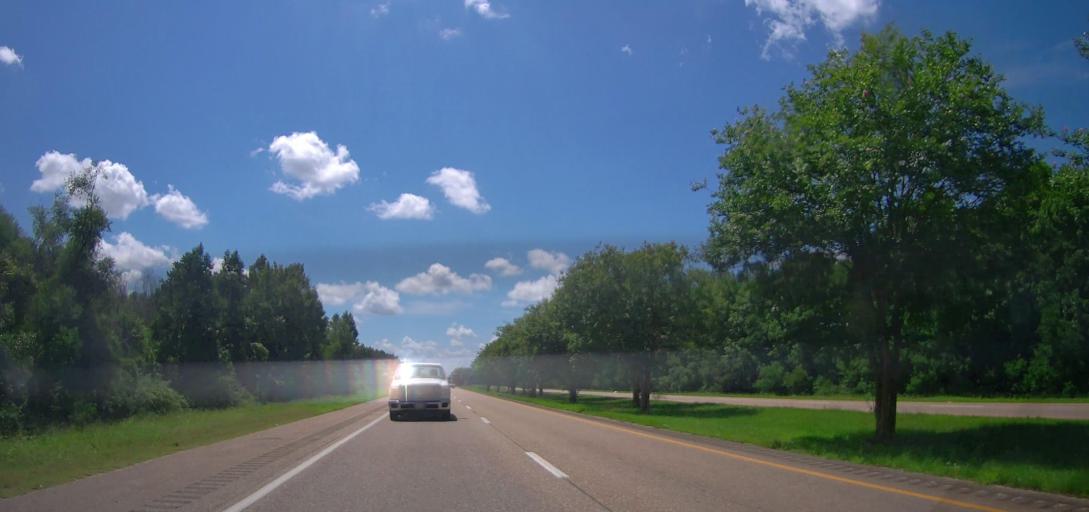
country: US
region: Alabama
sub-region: Montgomery County
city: Montgomery
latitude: 32.4220
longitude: -86.2458
